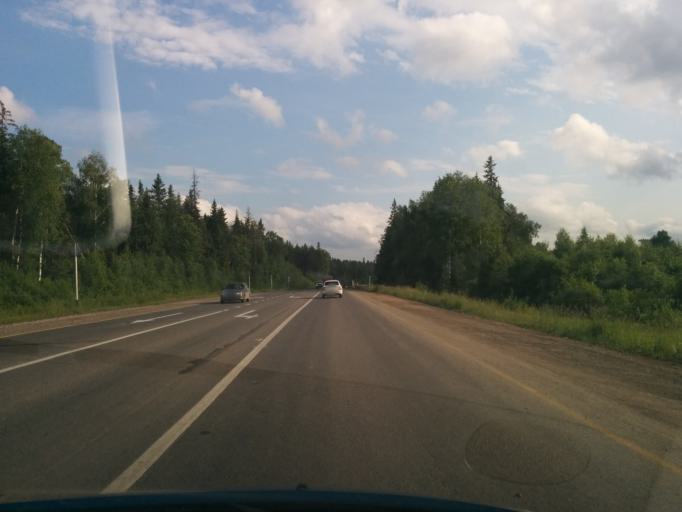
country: RU
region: Perm
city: Polazna
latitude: 58.1138
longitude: 56.4263
